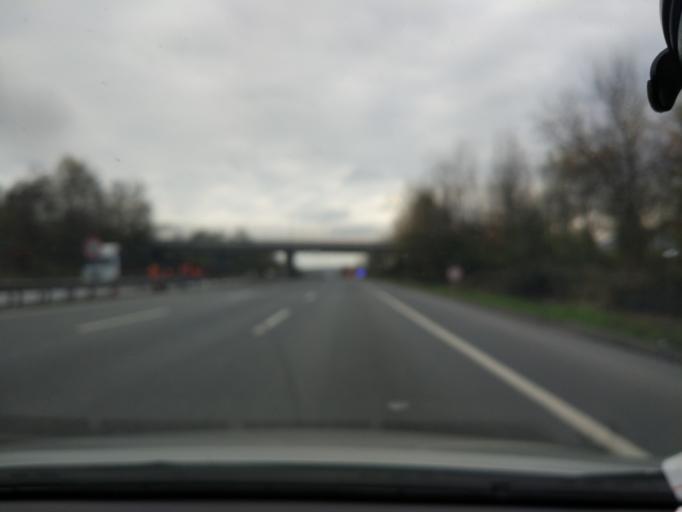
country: TR
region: Kocaeli
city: Derbent
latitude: 40.7259
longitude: 30.0803
